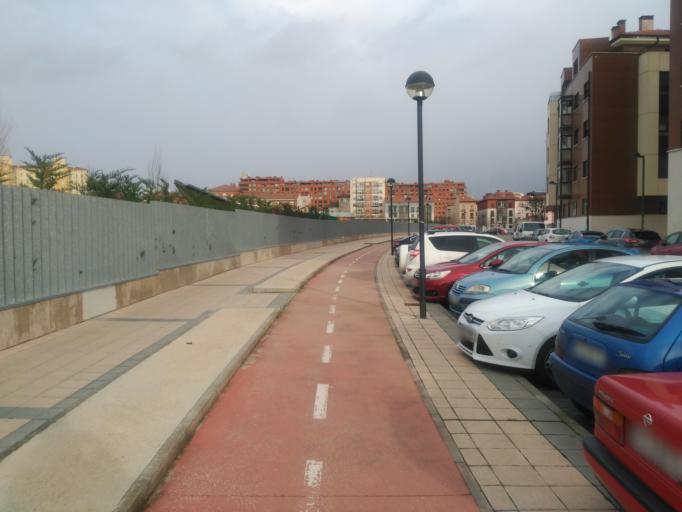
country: ES
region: Castille and Leon
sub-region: Provincia de Burgos
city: Burgos
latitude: 42.3337
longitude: -3.7068
